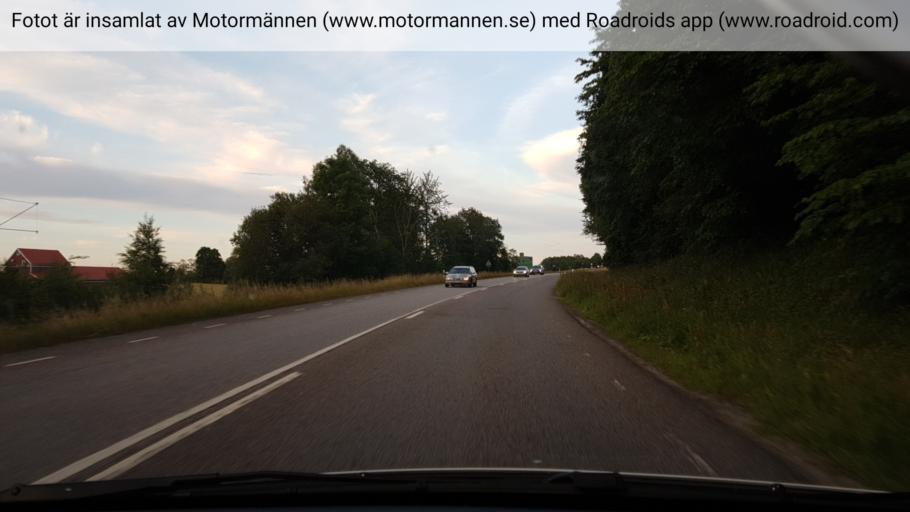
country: SE
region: Vaestra Goetaland
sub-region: Skovde Kommun
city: Skoevde
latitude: 58.3983
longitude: 13.9044
